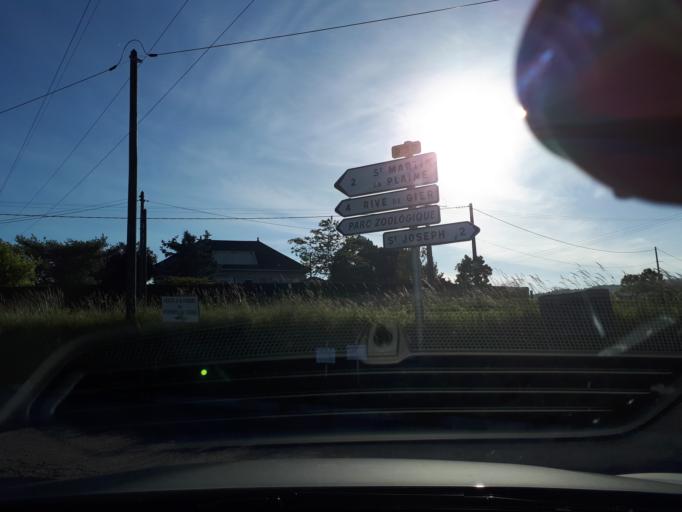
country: FR
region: Rhone-Alpes
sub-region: Departement de la Loire
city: Saint-Joseph
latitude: 45.5473
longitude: 4.6188
